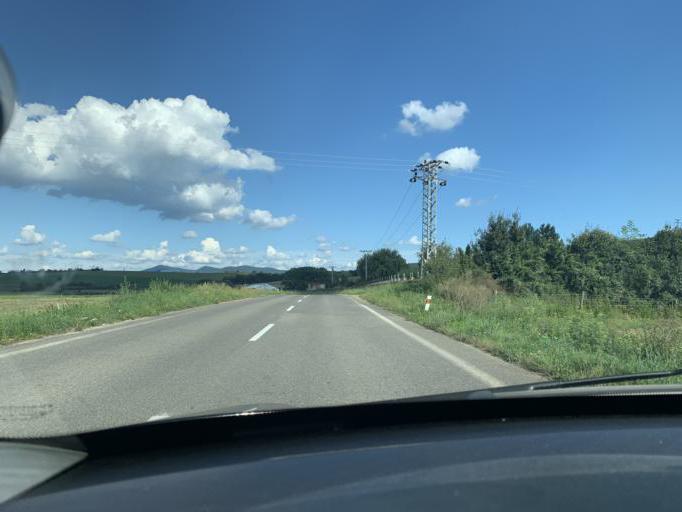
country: SK
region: Trenciansky
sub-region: Okres Trencin
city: Trencin
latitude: 48.8280
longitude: 17.9626
